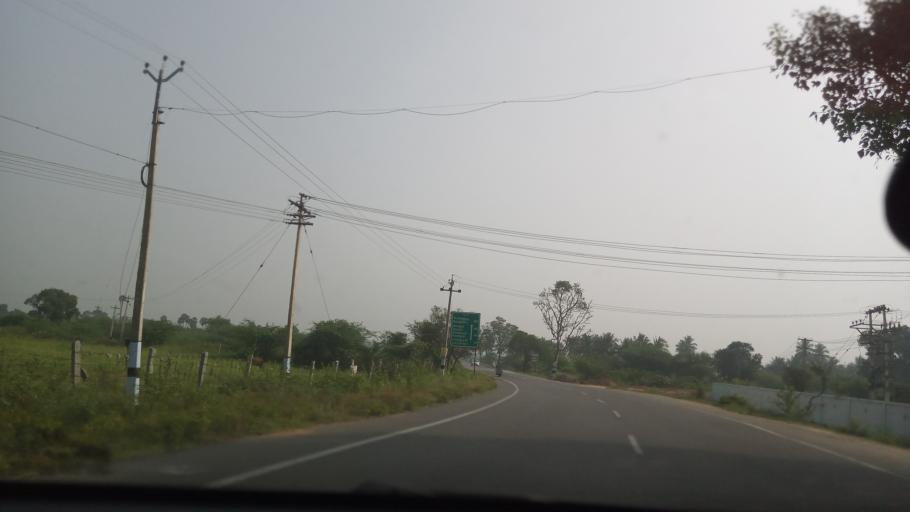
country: IN
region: Tamil Nadu
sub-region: Erode
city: Punjai Puliyampatti
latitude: 11.3859
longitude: 77.1759
